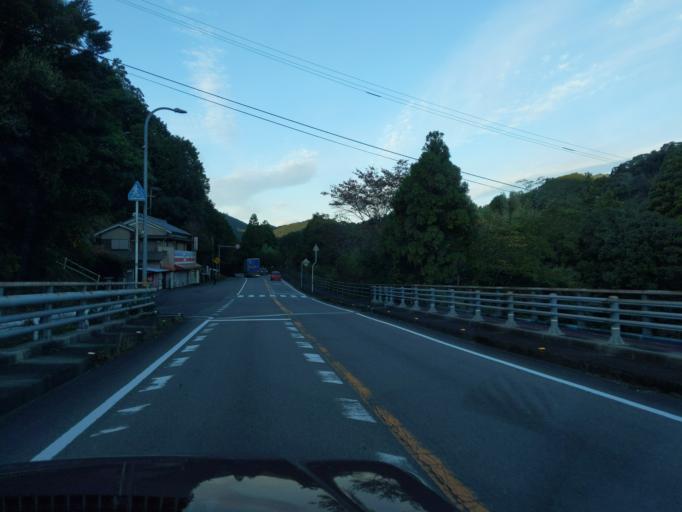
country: JP
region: Tokushima
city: Anan
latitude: 33.6917
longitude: 134.4343
